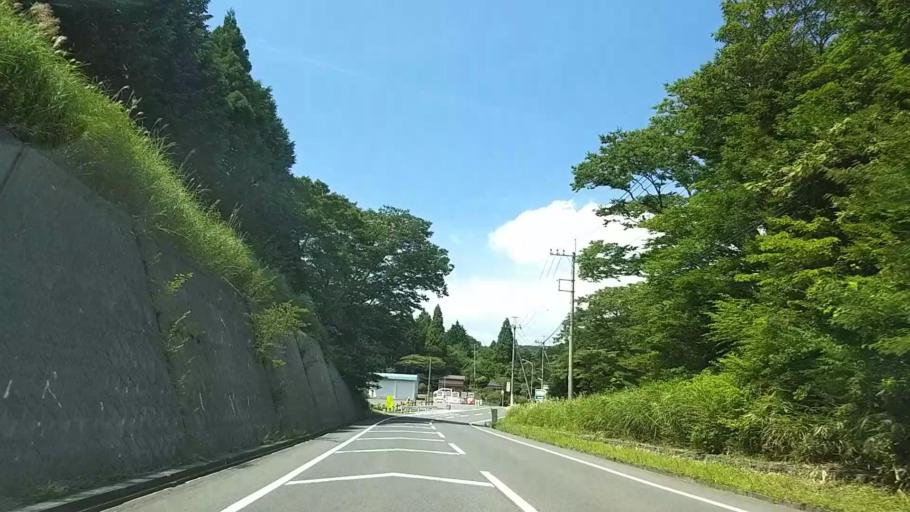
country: JP
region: Shizuoka
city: Fuji
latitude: 35.2560
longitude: 138.7908
